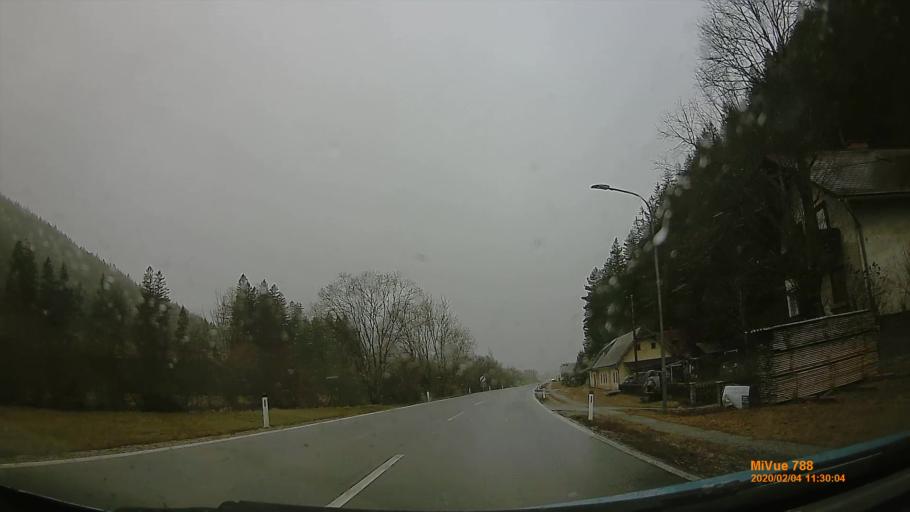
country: AT
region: Styria
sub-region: Politischer Bezirk Bruck-Muerzzuschlag
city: Kapellen
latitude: 47.6539
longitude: 15.6070
